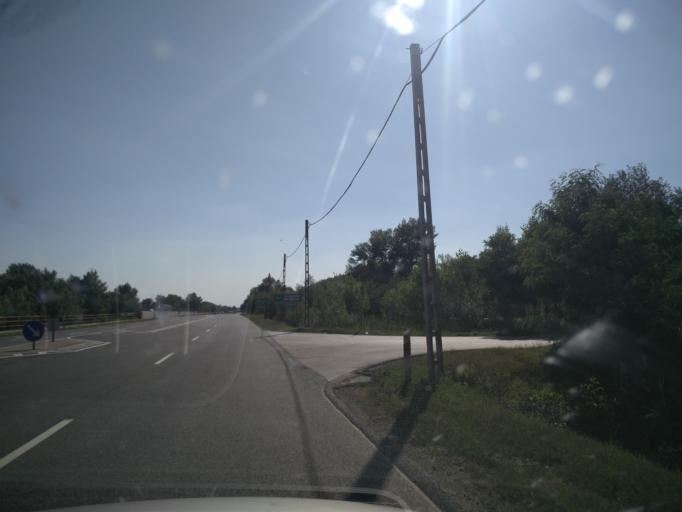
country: HU
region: Csongrad
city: Algyo
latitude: 46.3838
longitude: 20.2608
